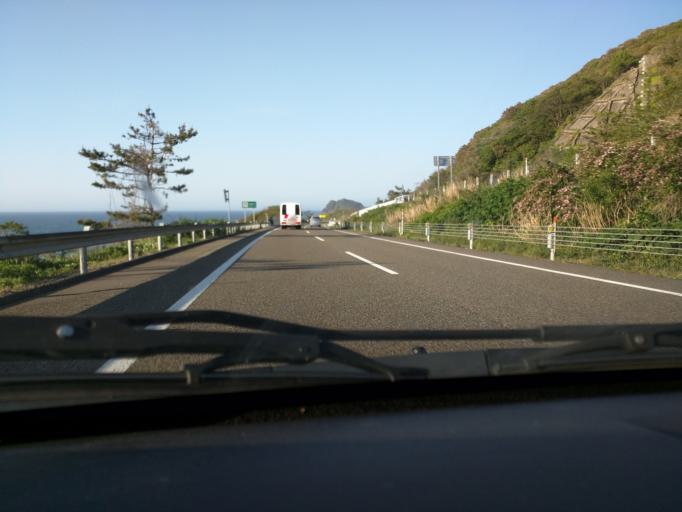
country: JP
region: Niigata
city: Kashiwazaki
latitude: 37.3045
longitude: 138.4188
